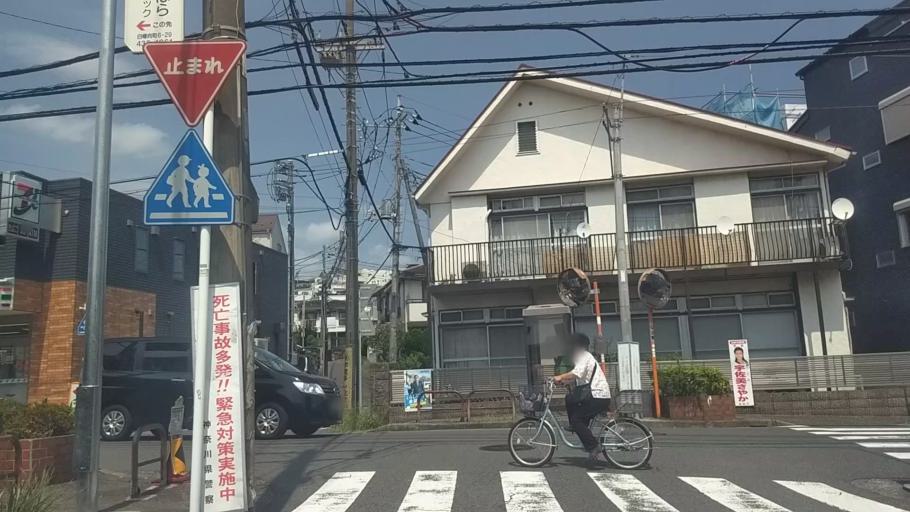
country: JP
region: Kanagawa
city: Yokohama
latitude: 35.4912
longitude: 139.6337
